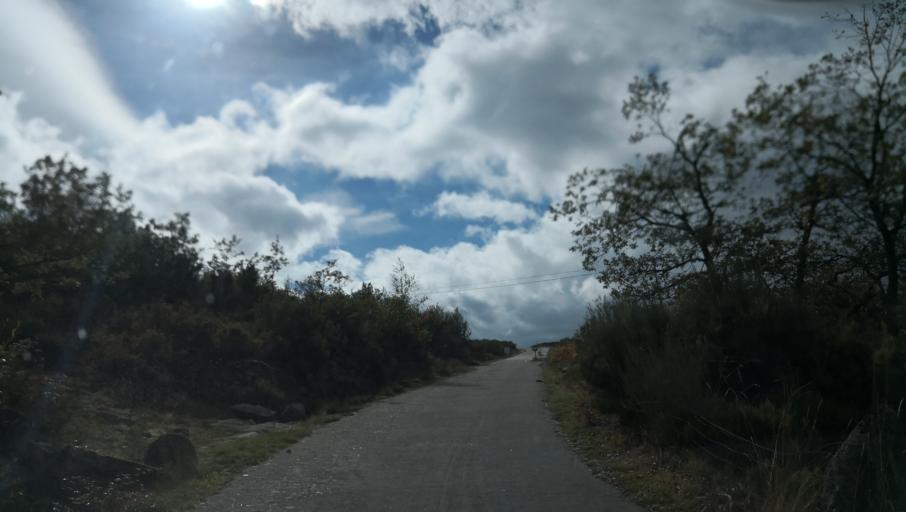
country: PT
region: Vila Real
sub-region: Vila Real
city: Vila Real
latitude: 41.3622
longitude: -7.7947
